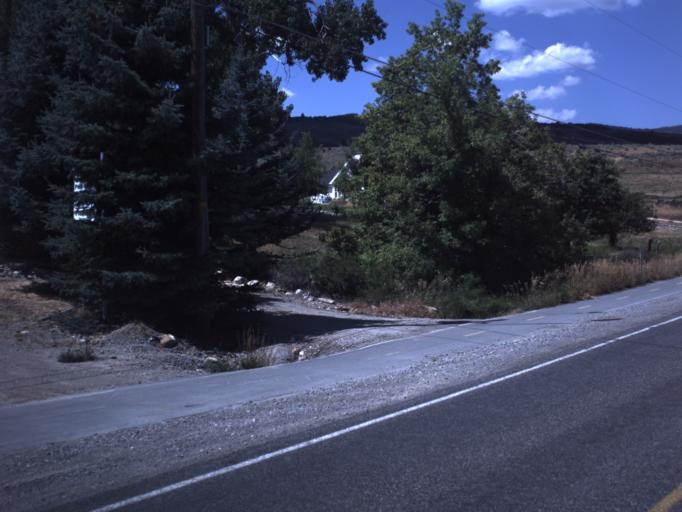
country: US
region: Idaho
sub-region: Bear Lake County
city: Paris
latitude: 41.9211
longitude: -111.3946
